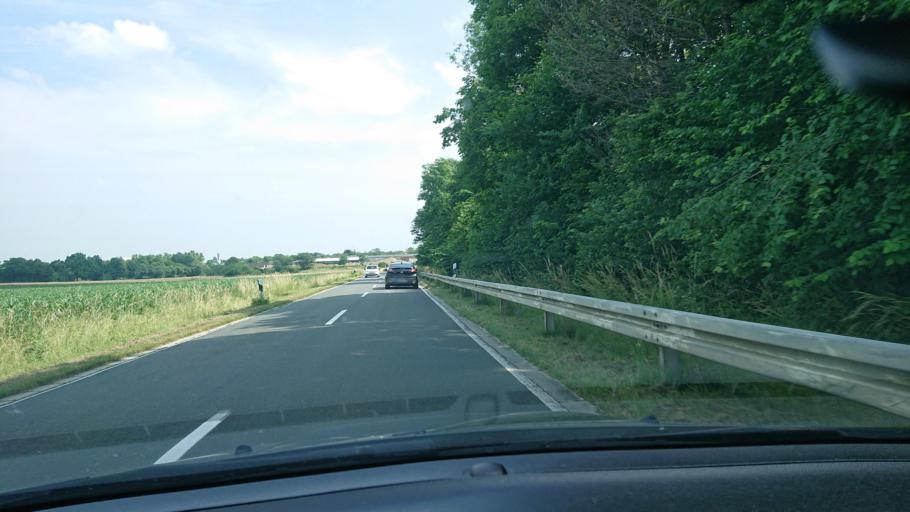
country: DE
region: North Rhine-Westphalia
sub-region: Regierungsbezirk Arnsberg
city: Soest
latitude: 51.5522
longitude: 8.0788
